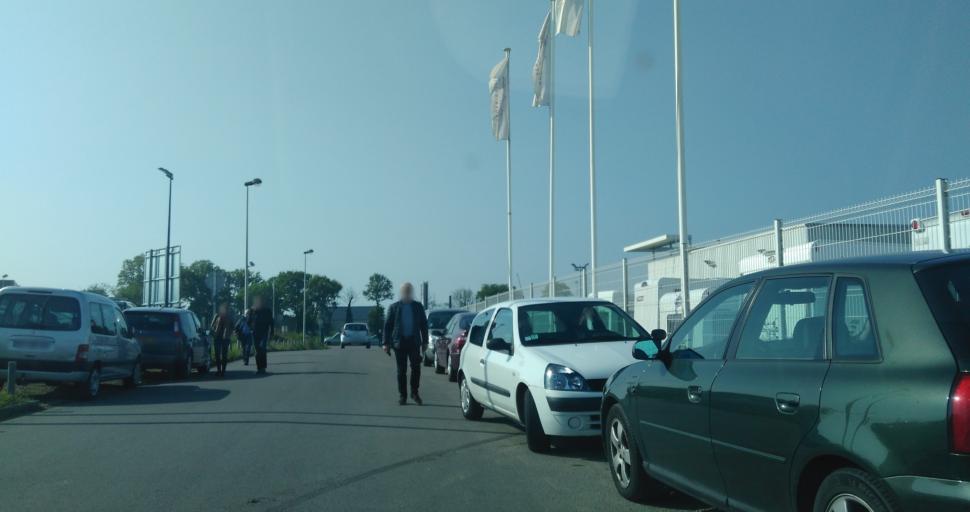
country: FR
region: Brittany
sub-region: Departement d'Ille-et-Vilaine
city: La Chapelle-des-Fougeretz
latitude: 48.1948
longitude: -1.7287
